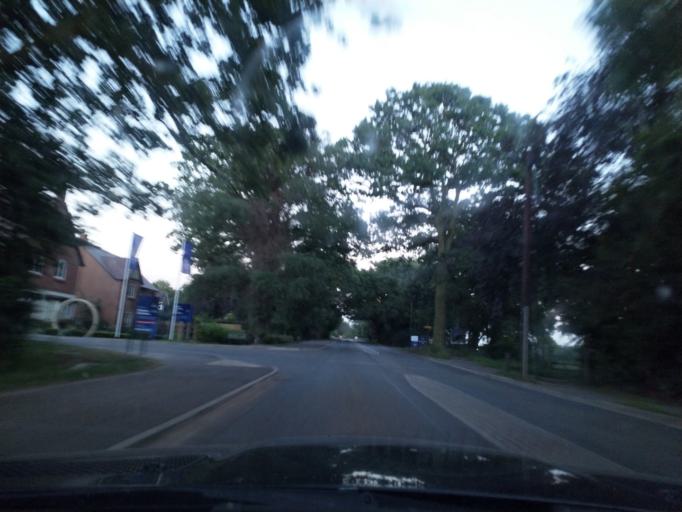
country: GB
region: England
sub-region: Solihull
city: Balsall Common
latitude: 52.3825
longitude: -1.6430
